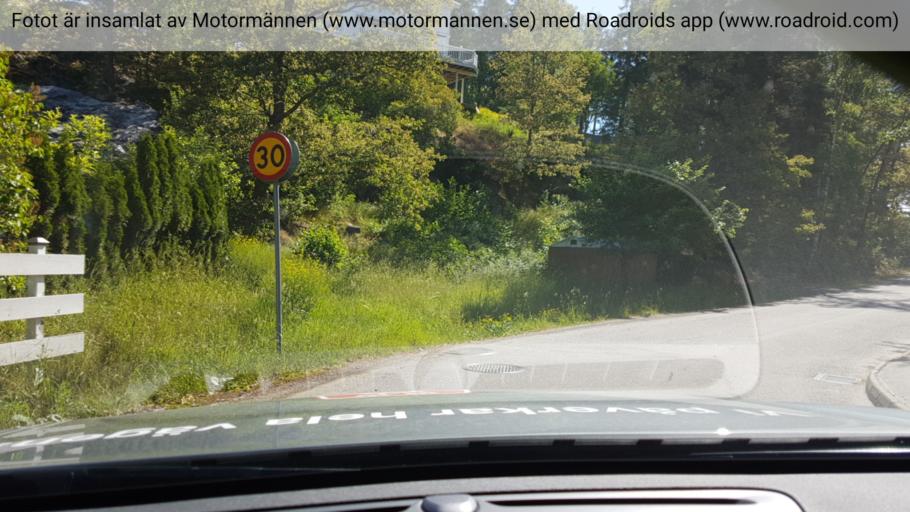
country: SE
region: Stockholm
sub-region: Nacka Kommun
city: Fisksatra
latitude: 59.2506
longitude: 18.2761
